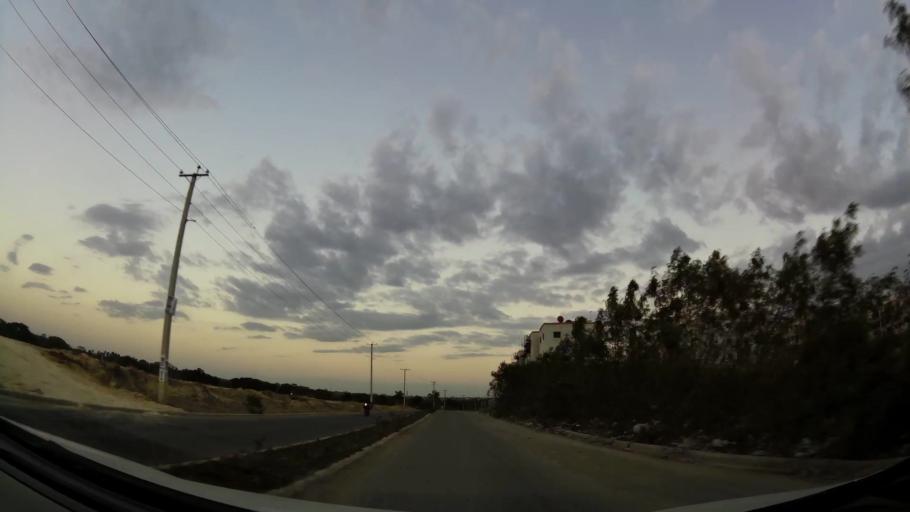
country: DO
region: Nacional
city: La Agustina
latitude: 18.5626
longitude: -69.9395
